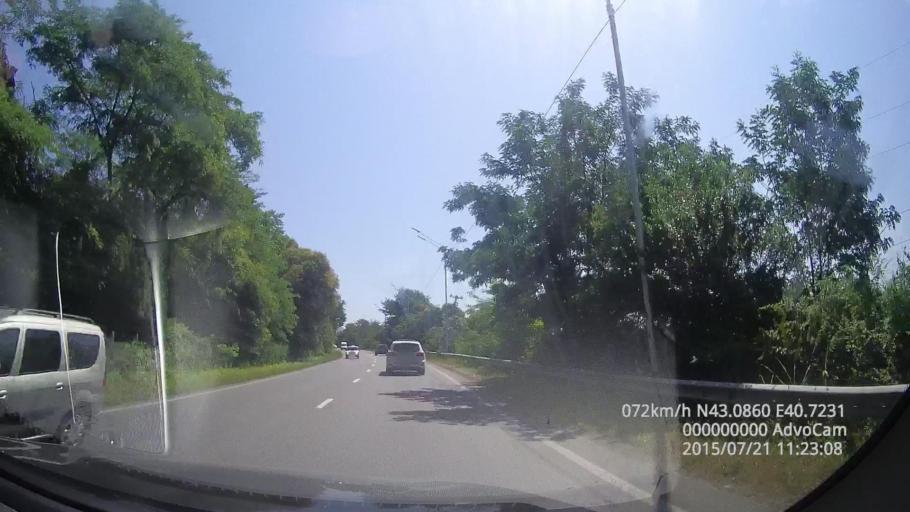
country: GE
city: P'rimorsk'oe
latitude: 43.0860
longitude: 40.7235
